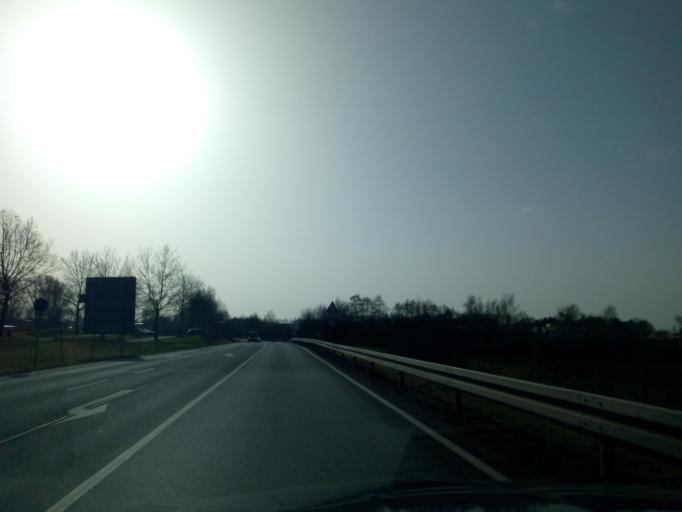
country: DE
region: Saarland
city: Saarwellingen
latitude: 49.3289
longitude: 6.8126
